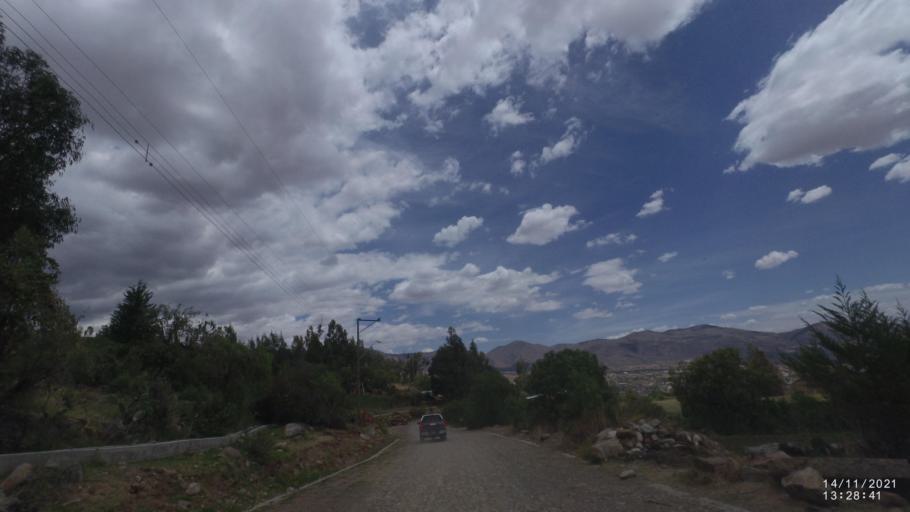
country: BO
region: Cochabamba
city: Colomi
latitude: -17.3857
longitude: -65.9855
